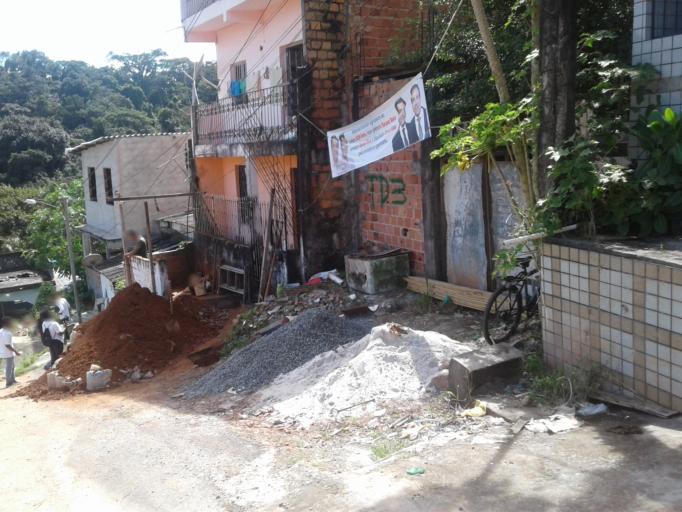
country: BR
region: Bahia
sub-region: Salvador
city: Salvador
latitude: -12.9114
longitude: -38.4686
